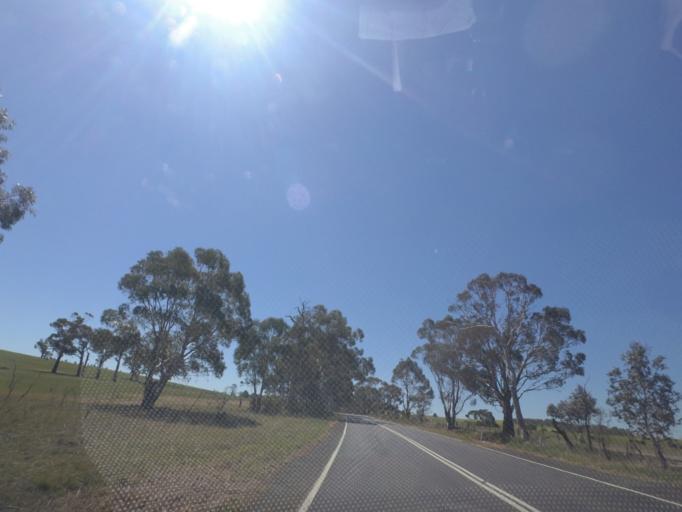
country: AU
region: Victoria
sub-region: Hume
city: Sunbury
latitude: -37.1520
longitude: 144.7712
